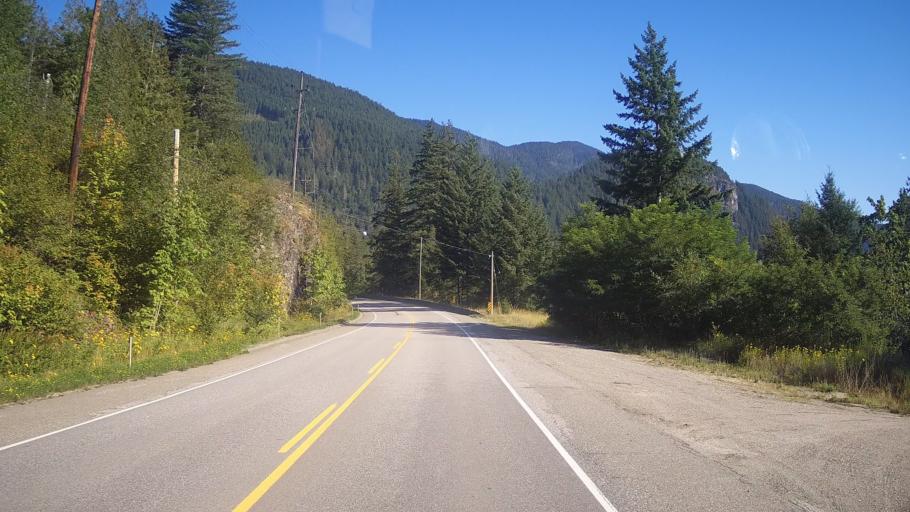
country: CA
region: British Columbia
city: Hope
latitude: 49.5482
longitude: -121.4412
